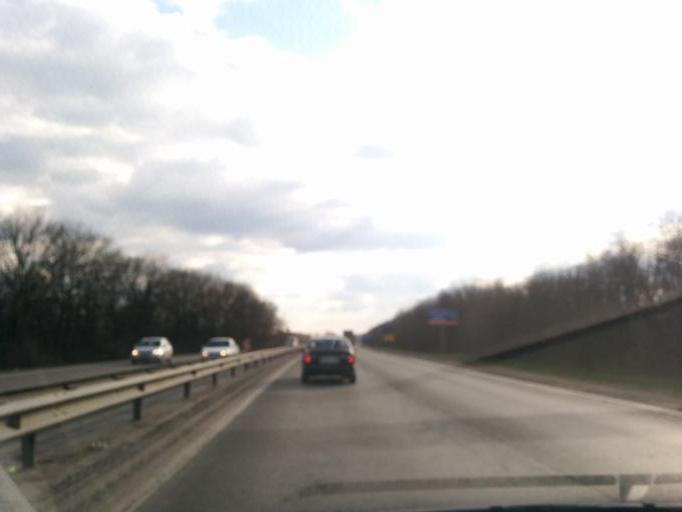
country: RU
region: Rostov
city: Grushevskaya
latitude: 47.3706
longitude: 39.9014
